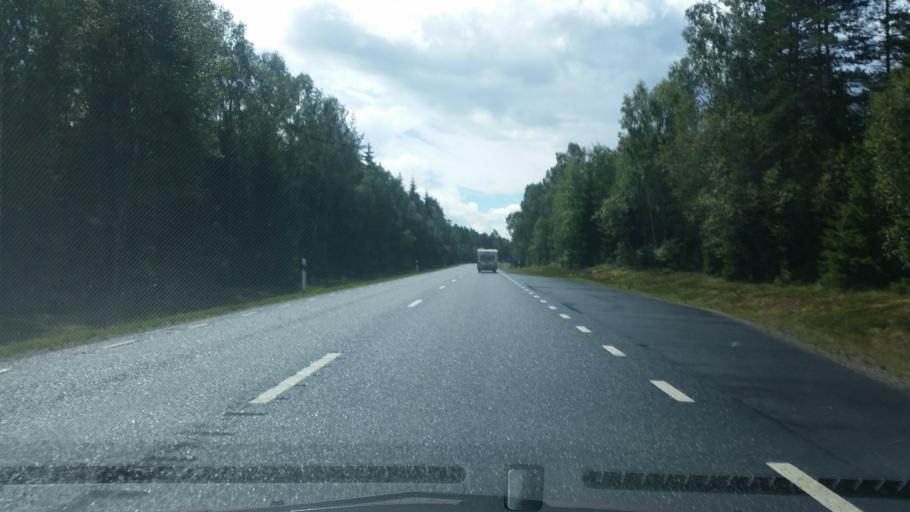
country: SE
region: Joenkoeping
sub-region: Gislaveds Kommun
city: Gislaved
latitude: 57.3918
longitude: 13.5899
